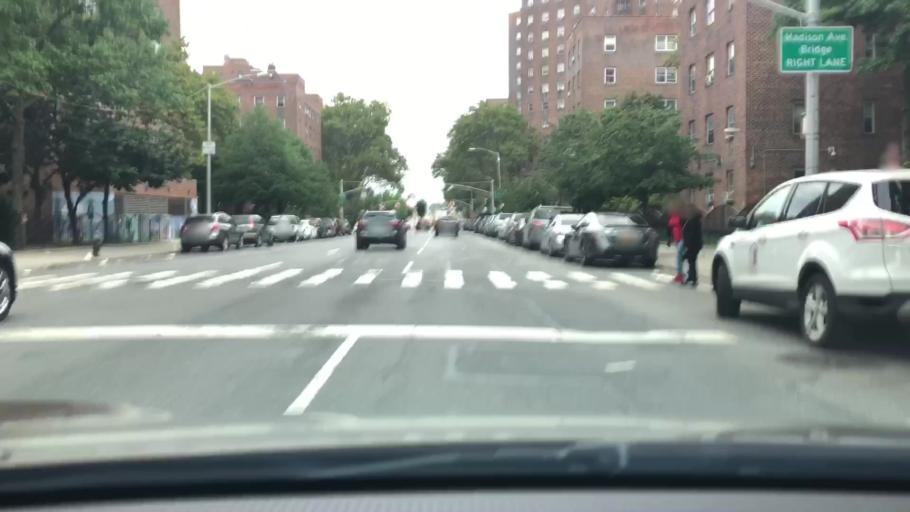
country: US
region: New York
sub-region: New York County
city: Manhattan
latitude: 40.8108
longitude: -73.9370
